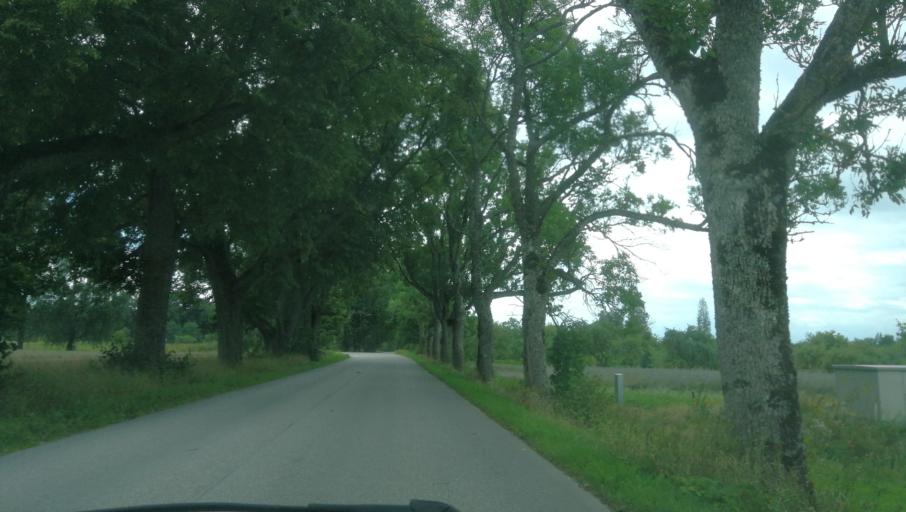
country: LV
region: Priekuli
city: Priekuli
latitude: 57.3740
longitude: 25.4355
